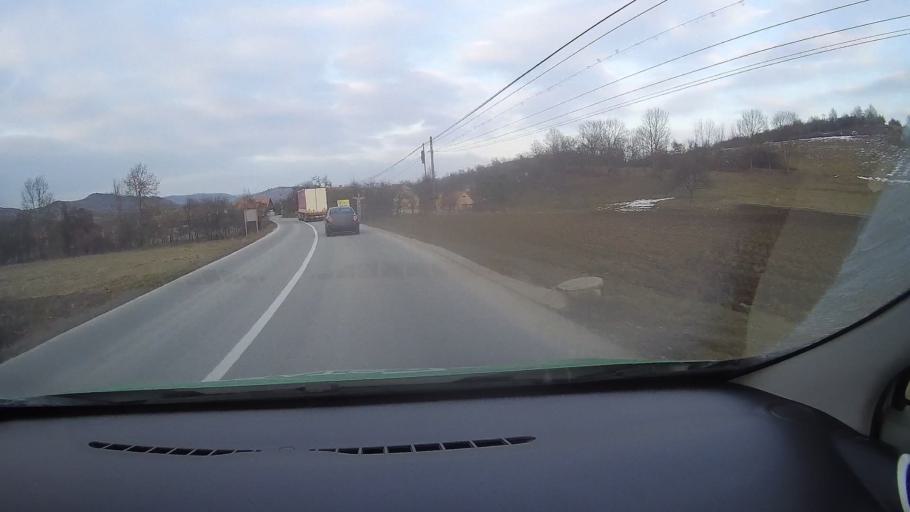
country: RO
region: Harghita
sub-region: Comuna Simonesti
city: Simonesti
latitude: 46.3446
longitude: 25.1183
